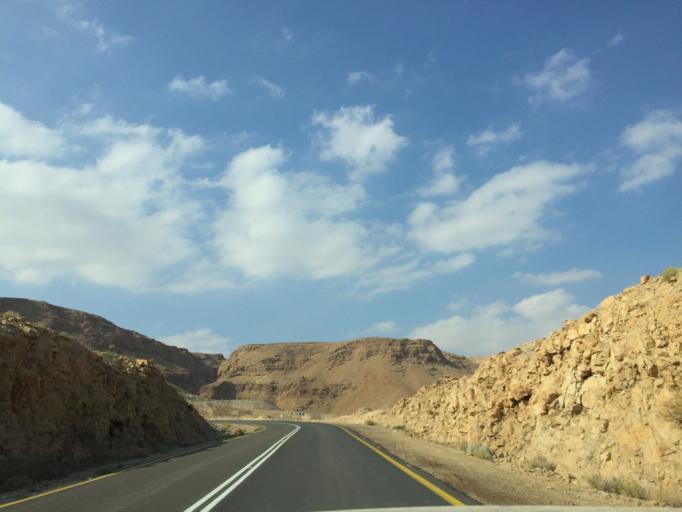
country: IL
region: Southern District
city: `En Boqeq
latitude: 31.3214
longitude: 35.3387
